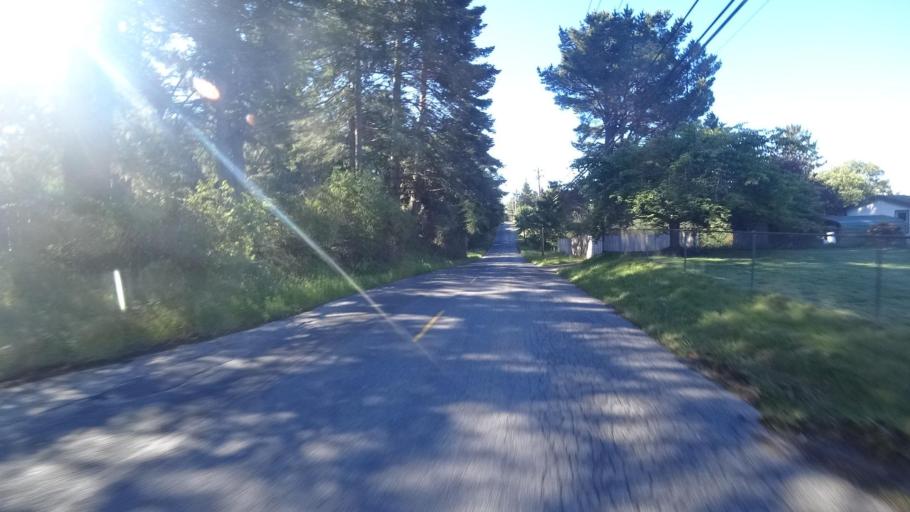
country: US
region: California
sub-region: Humboldt County
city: McKinleyville
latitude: 40.9693
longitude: -124.0959
